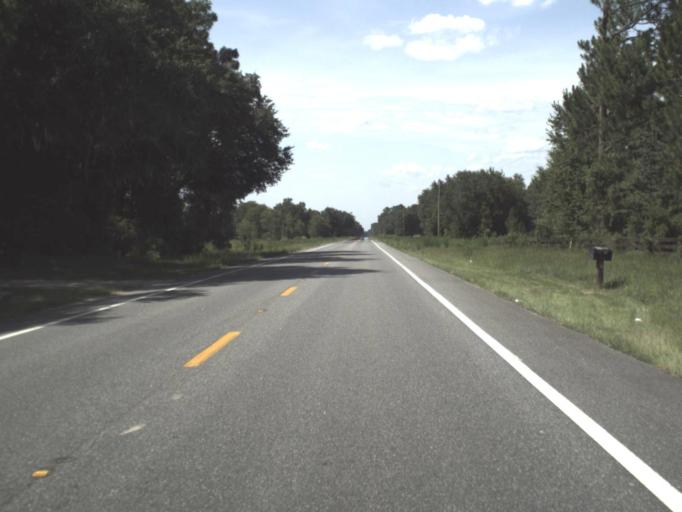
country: US
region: Florida
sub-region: Alachua County
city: High Springs
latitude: 29.8240
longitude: -82.7415
